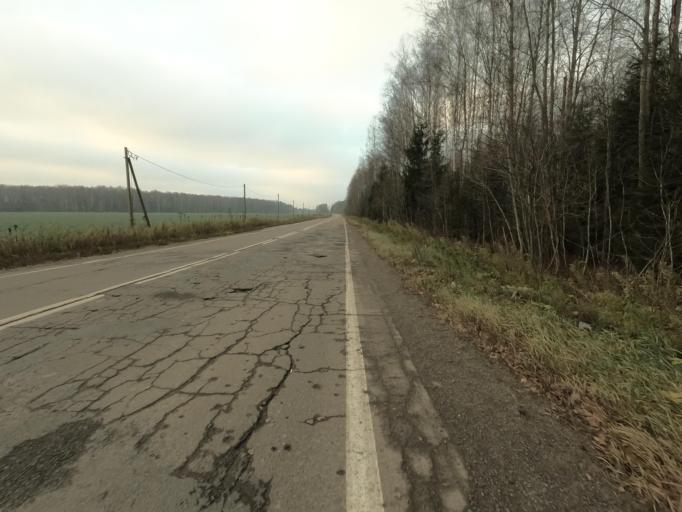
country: RU
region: Leningrad
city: Mga
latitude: 59.7968
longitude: 31.0030
